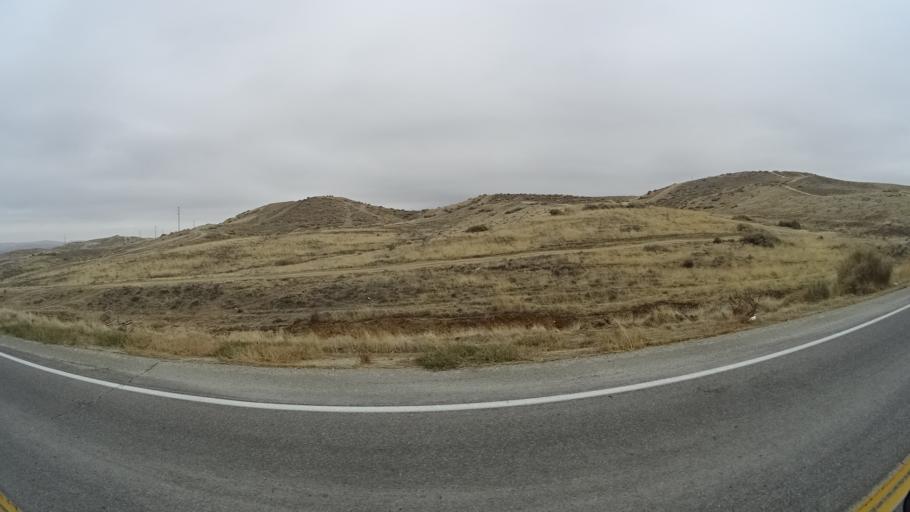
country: US
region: California
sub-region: Kern County
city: Oildale
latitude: 35.4166
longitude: -118.9387
